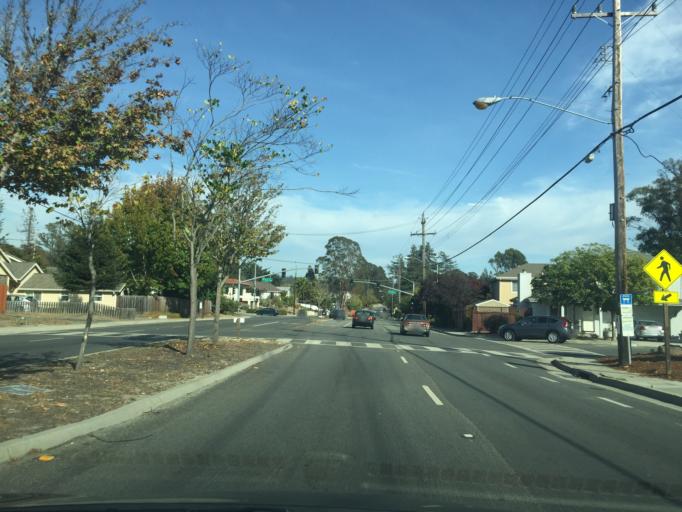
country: US
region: California
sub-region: Santa Cruz County
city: Soquel
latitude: 36.9876
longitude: -121.9474
